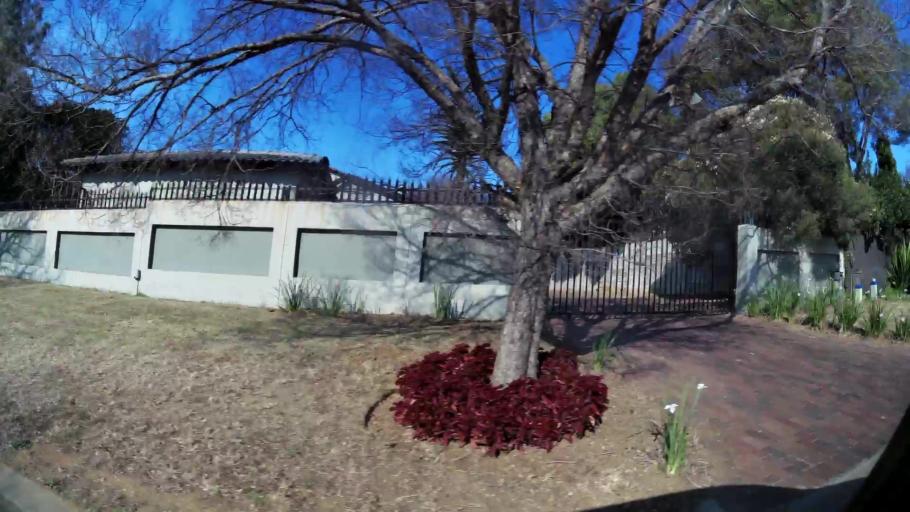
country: ZA
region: Gauteng
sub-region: City of Johannesburg Metropolitan Municipality
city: Roodepoort
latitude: -26.0984
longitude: 27.9735
